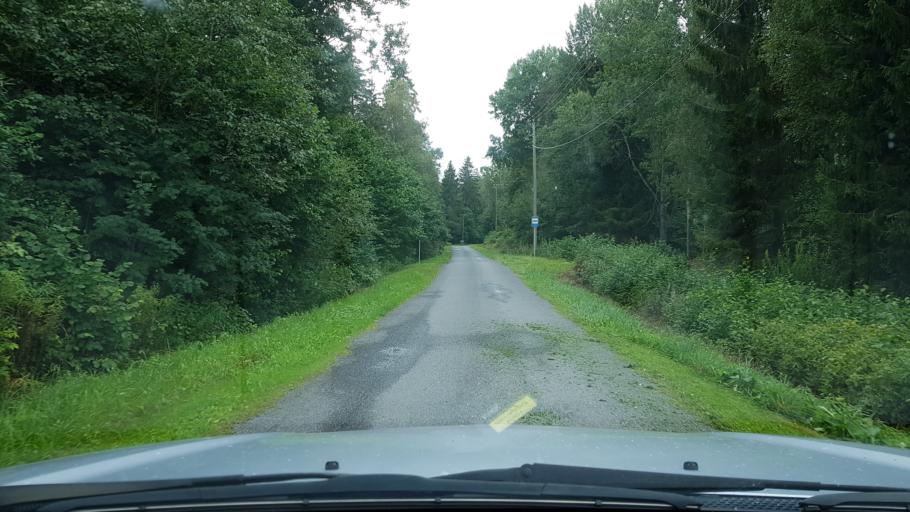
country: EE
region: Harju
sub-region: Raasiku vald
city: Arukula
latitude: 59.3017
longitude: 25.0526
